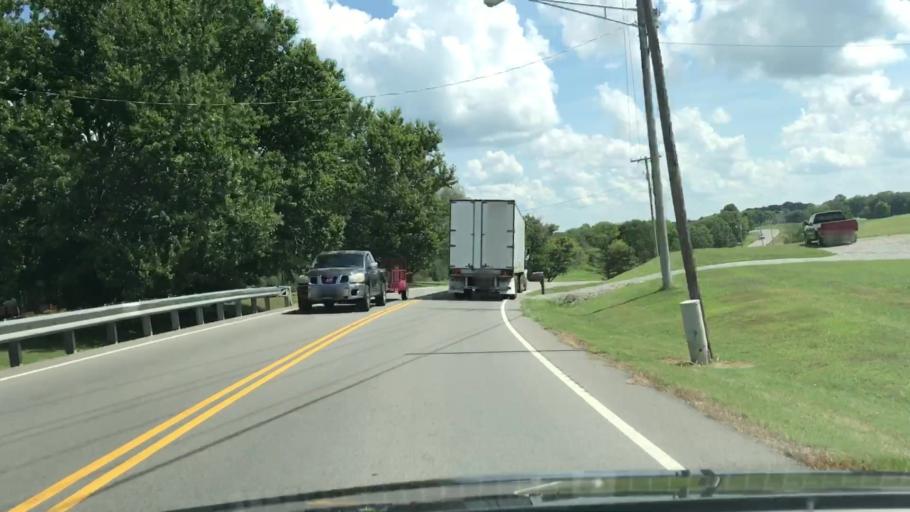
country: US
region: Tennessee
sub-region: Robertson County
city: Cross Plains
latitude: 36.5407
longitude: -86.6694
